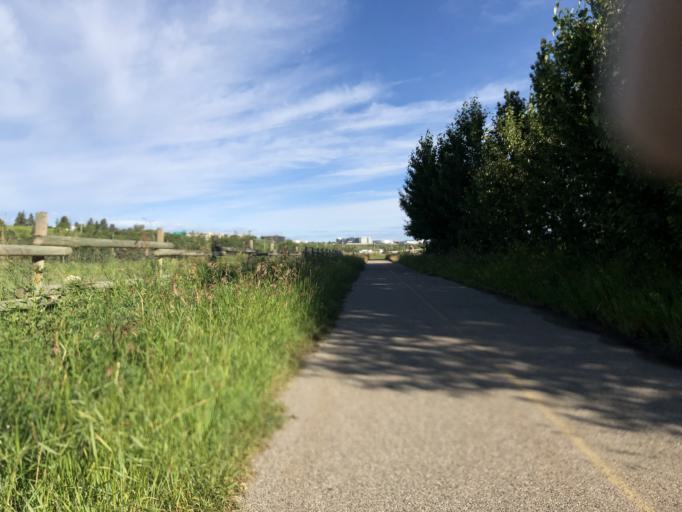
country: CA
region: Alberta
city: Calgary
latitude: 50.9716
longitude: -114.0353
